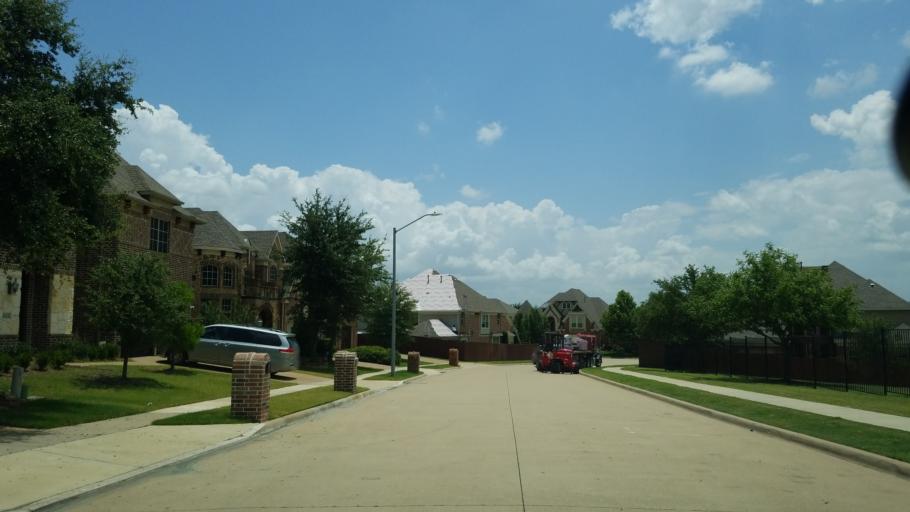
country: US
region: Texas
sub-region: Dallas County
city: Coppell
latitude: 32.9438
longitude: -96.9633
